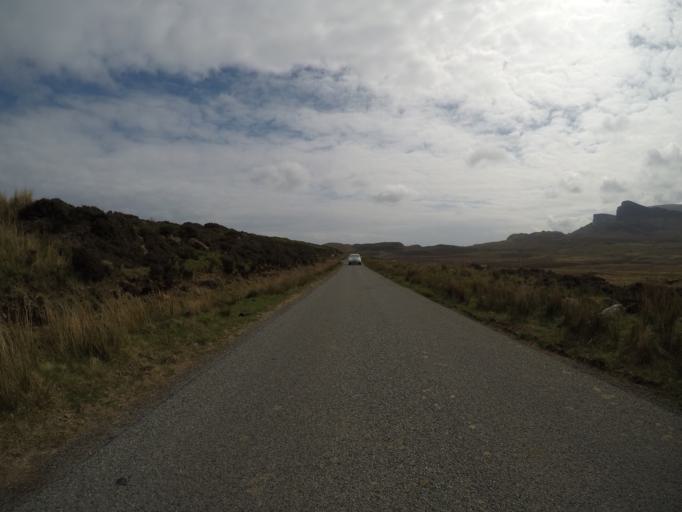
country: GB
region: Scotland
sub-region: Highland
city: Portree
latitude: 57.6791
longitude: -6.2743
